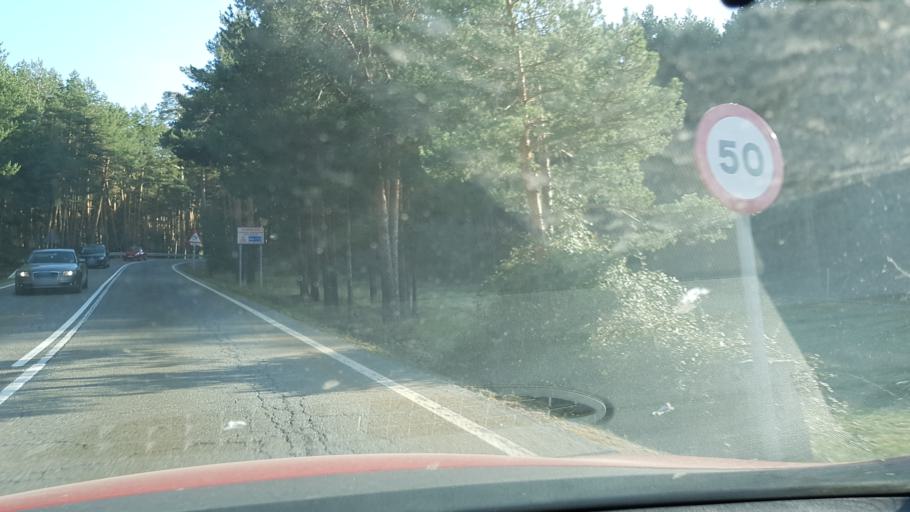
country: ES
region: Castille and Leon
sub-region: Provincia de Segovia
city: San Ildefonso
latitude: 40.8229
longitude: -4.0172
